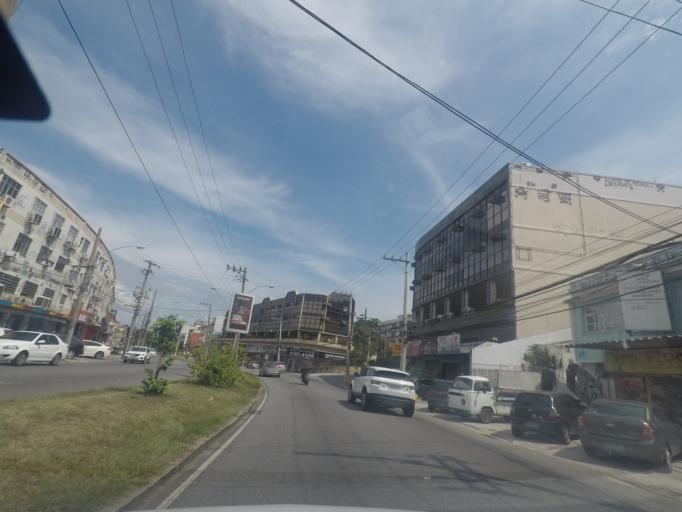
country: BR
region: Rio de Janeiro
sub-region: Rio De Janeiro
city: Rio de Janeiro
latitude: -22.8103
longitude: -43.1951
